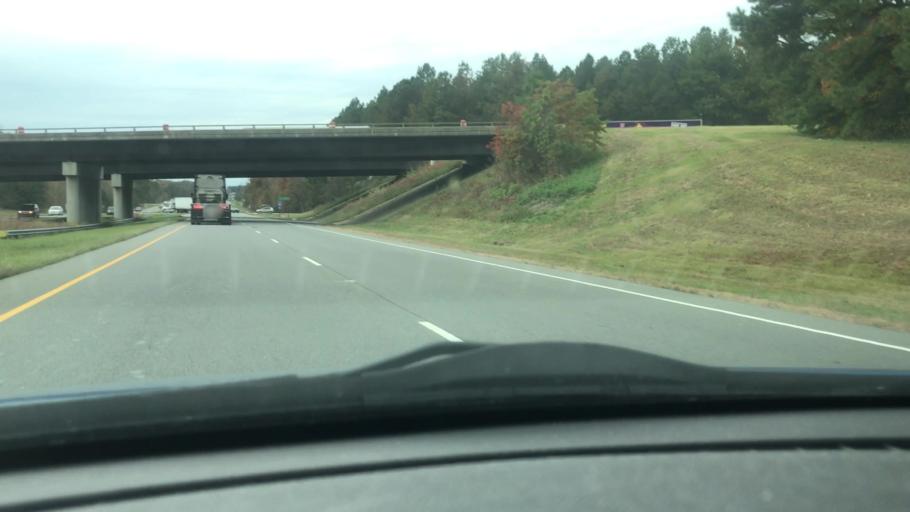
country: US
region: North Carolina
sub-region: Davidson County
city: Lexington
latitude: 35.8095
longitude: -80.1812
